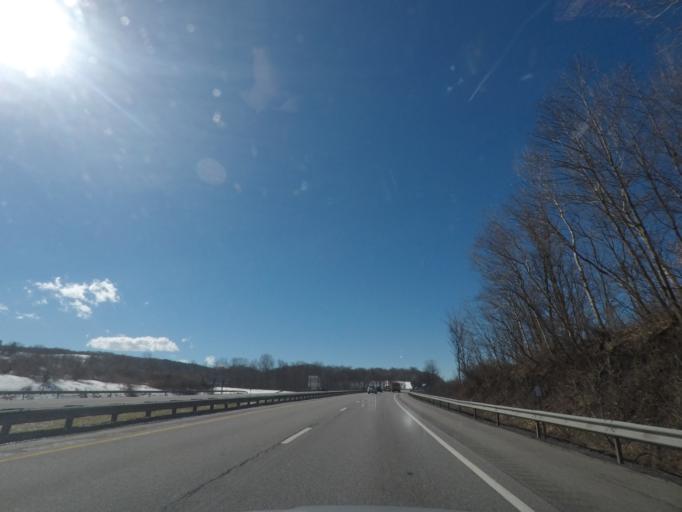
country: US
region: New York
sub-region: Herkimer County
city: Little Falls
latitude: 43.0103
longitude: -74.8393
